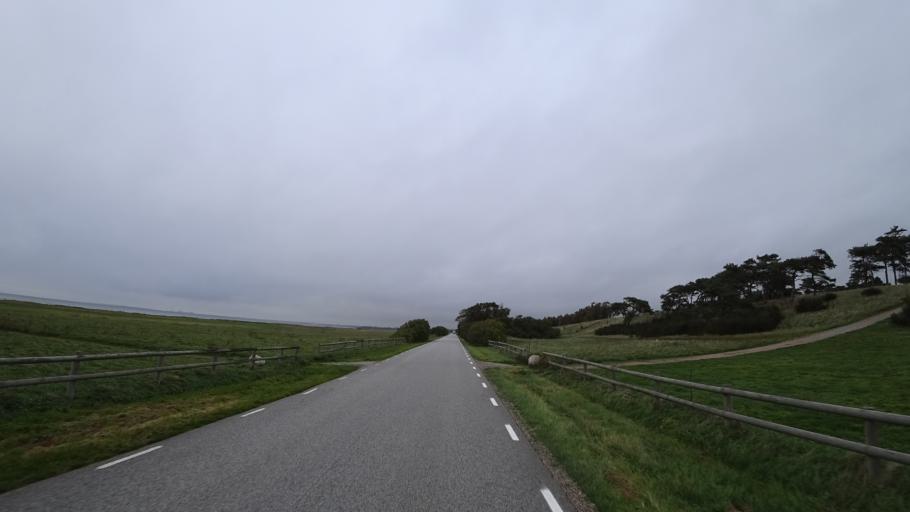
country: SE
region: Skane
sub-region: Kavlinge Kommun
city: Hofterup
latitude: 55.7923
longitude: 12.9381
